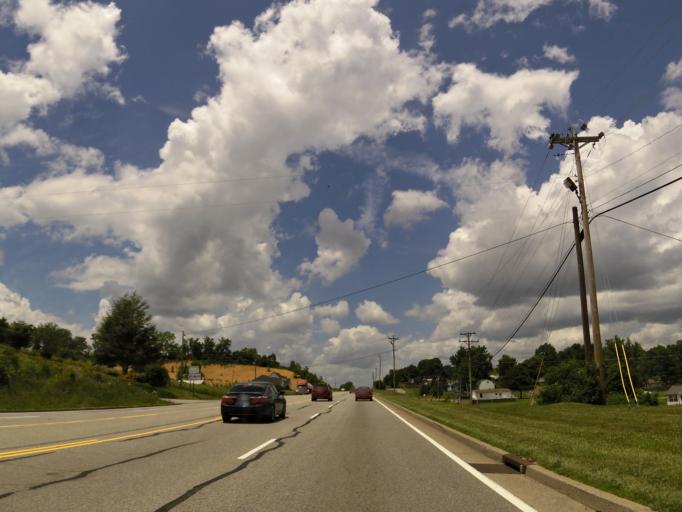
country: US
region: Tennessee
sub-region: Claiborne County
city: Tazewell
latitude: 36.4753
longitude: -83.5800
